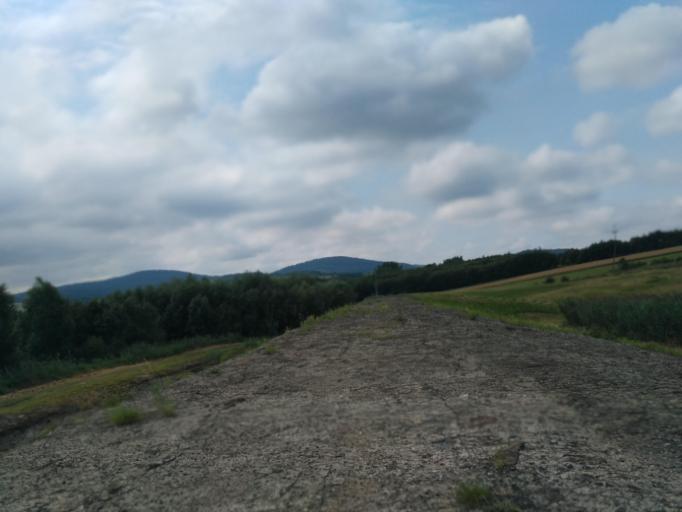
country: PL
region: Subcarpathian Voivodeship
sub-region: Powiat krosnienski
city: Rymanow
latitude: 49.5936
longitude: 21.8436
